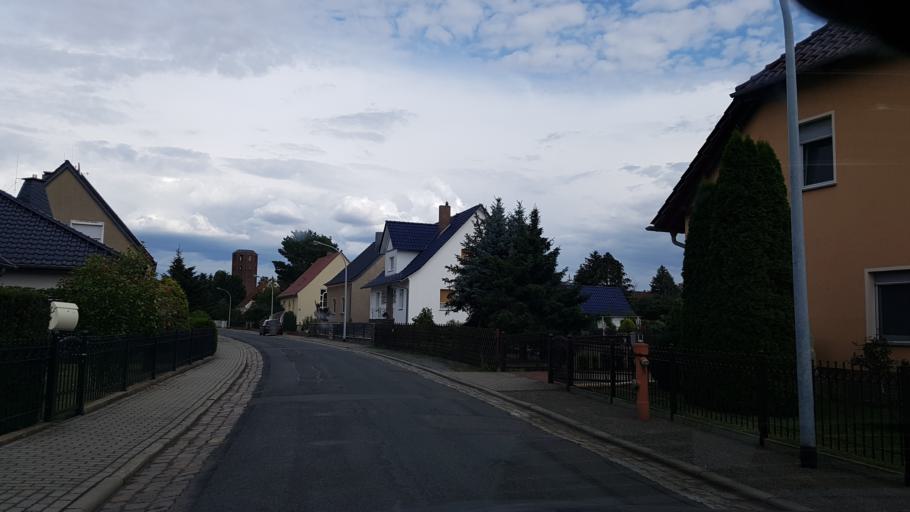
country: DE
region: Brandenburg
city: Falkenberg
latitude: 51.5806
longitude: 13.2398
